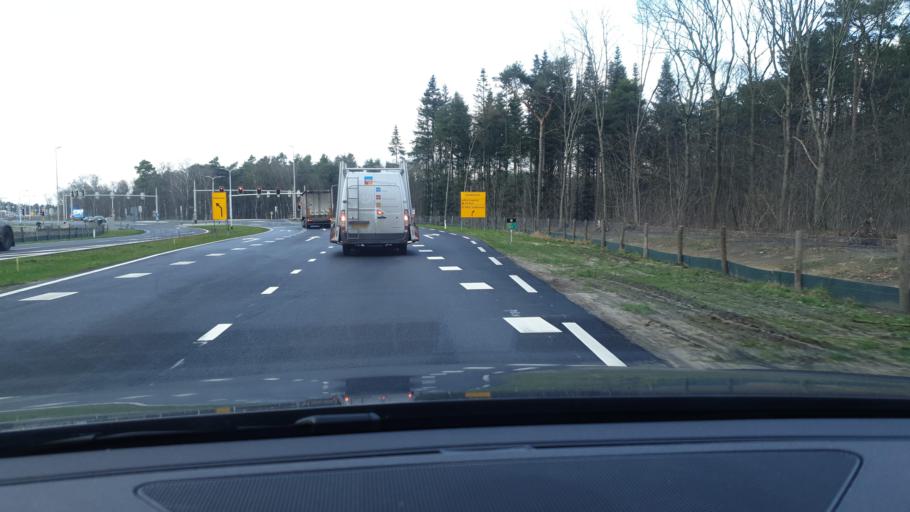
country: NL
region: North Brabant
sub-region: Gemeente Veldhoven
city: Veldhoven
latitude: 51.3904
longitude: 5.3858
